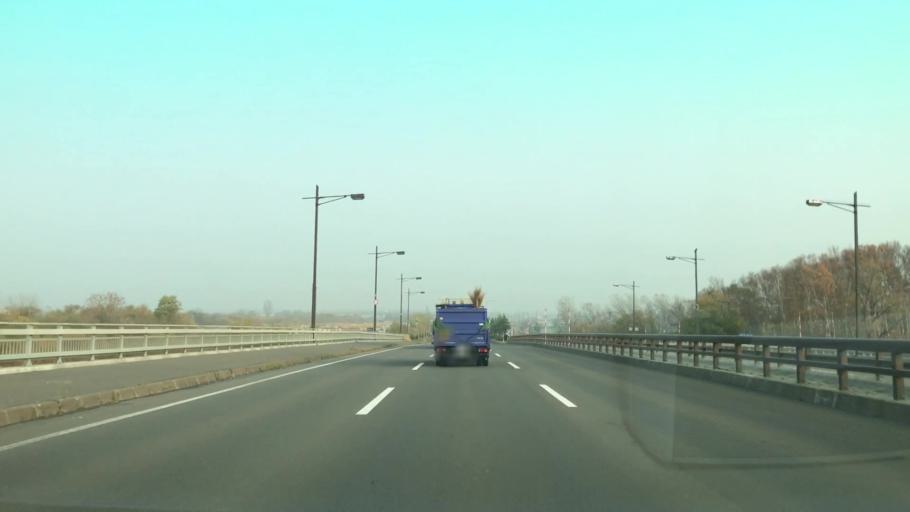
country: JP
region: Hokkaido
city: Ishikari
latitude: 43.1683
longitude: 141.3485
